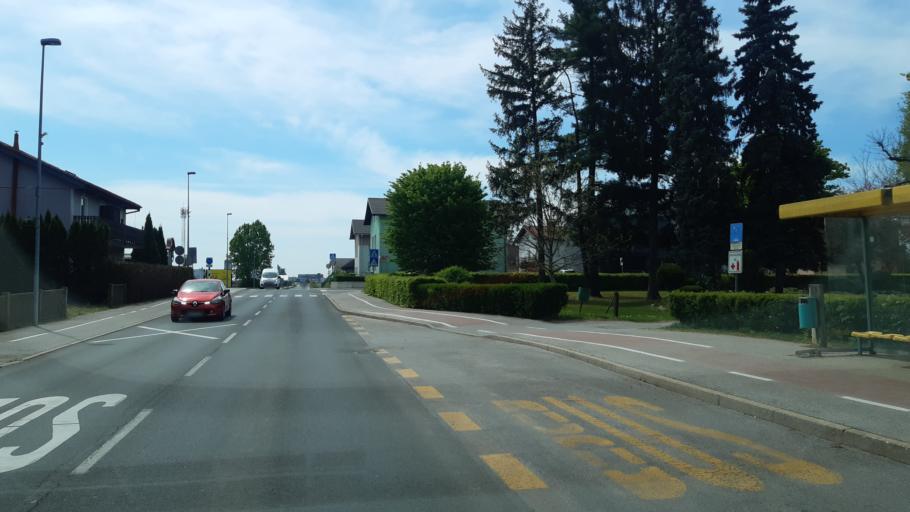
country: SI
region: Murska Sobota
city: Murska Sobota
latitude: 46.6545
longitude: 16.1698
